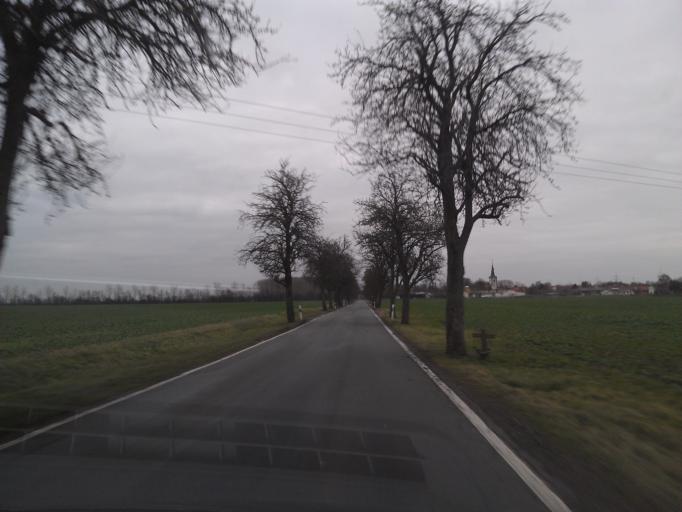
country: DE
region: Thuringia
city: Pferdingsleben
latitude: 50.9746
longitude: 10.8092
